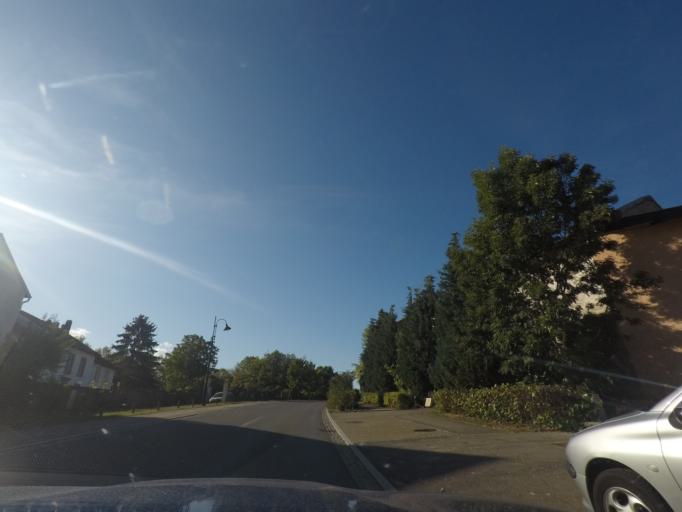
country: FR
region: Lorraine
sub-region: Departement de la Moselle
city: Hettange-Grande
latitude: 49.4558
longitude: 6.1788
